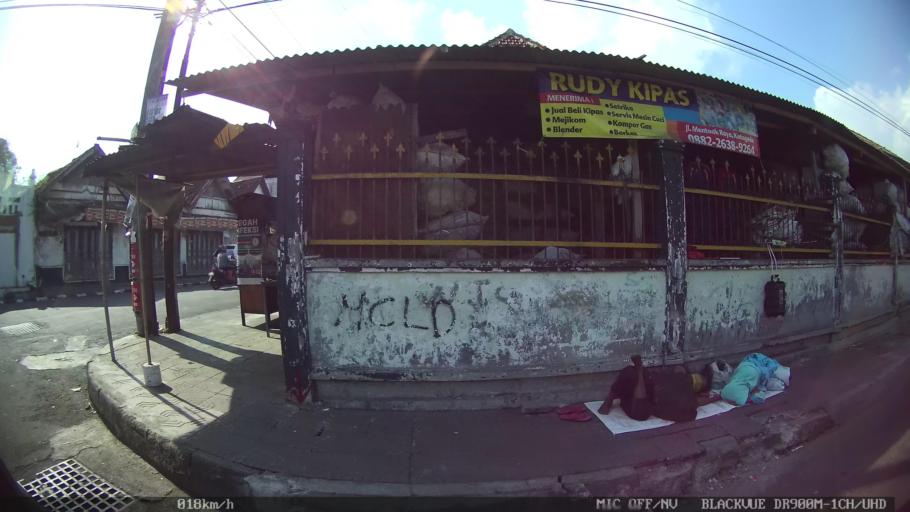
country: ID
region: Daerah Istimewa Yogyakarta
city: Yogyakarta
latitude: -7.8288
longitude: 110.3997
